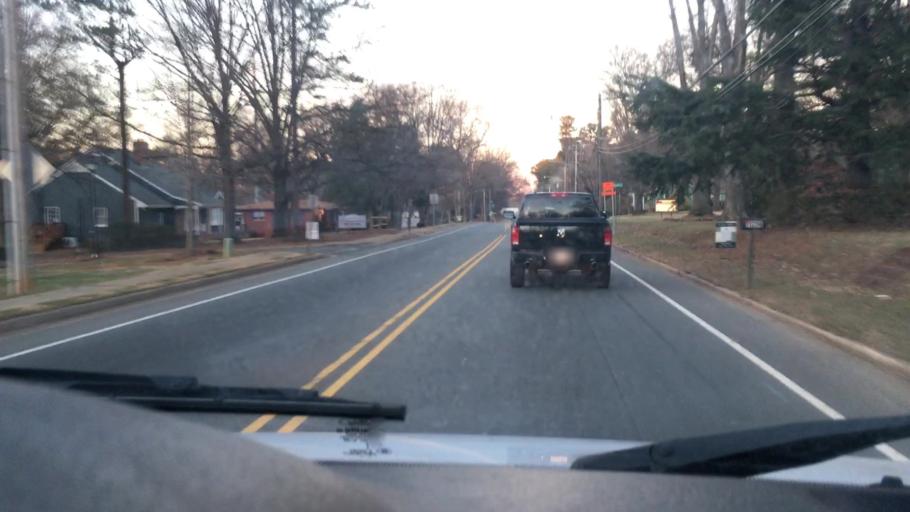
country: US
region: North Carolina
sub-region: Mecklenburg County
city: Huntersville
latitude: 35.4151
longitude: -80.8430
